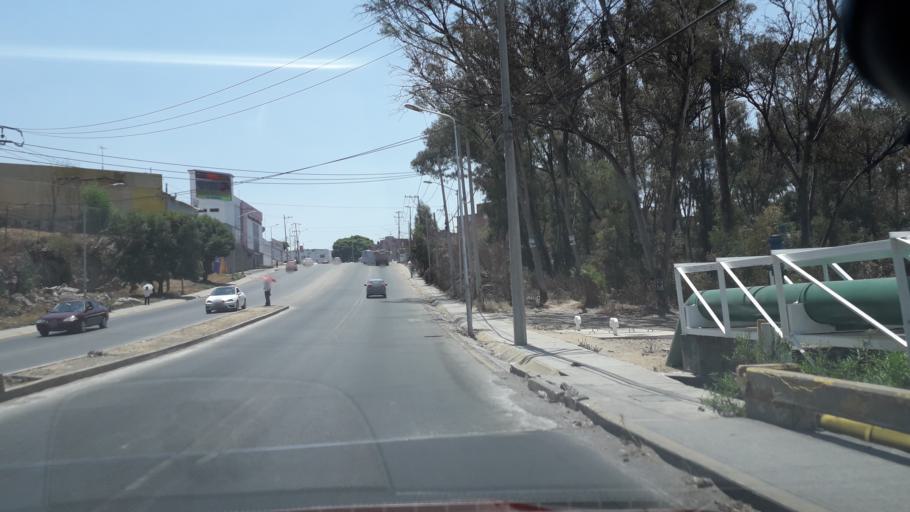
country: MX
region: Puebla
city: Puebla
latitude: 19.0116
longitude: -98.1895
